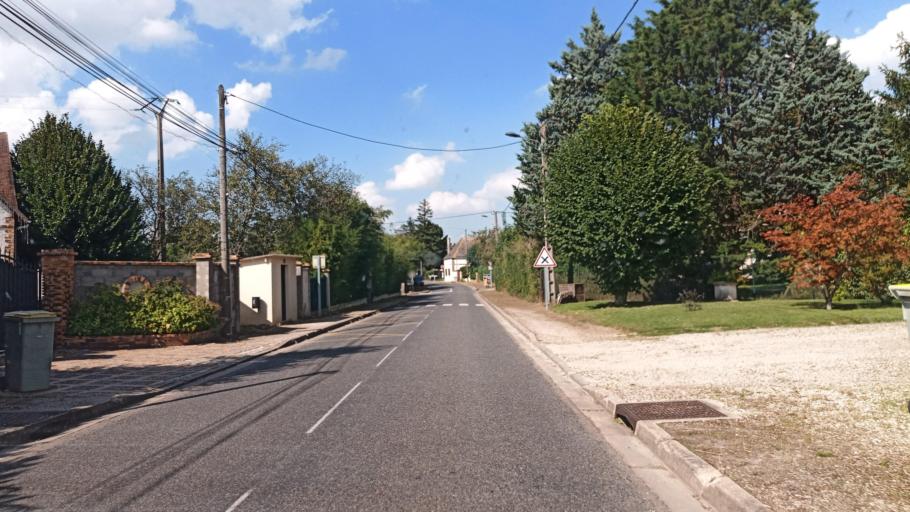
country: FR
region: Bourgogne
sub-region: Departement de l'Yonne
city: Saint-Valerien
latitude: 48.1454
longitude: 3.0897
